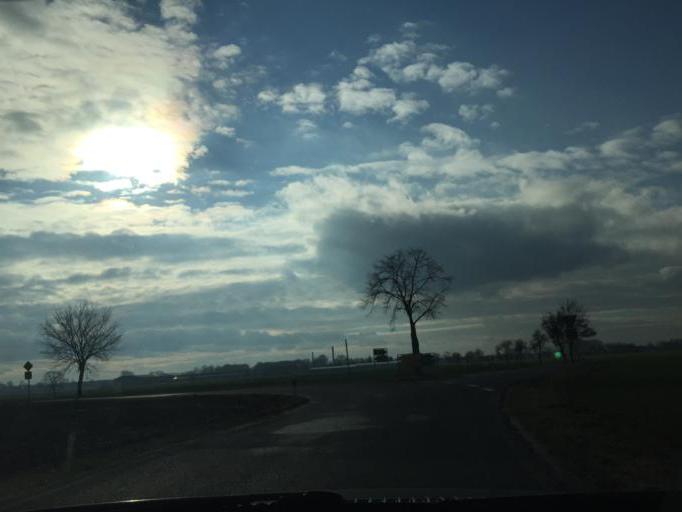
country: DE
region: Saxony
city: Schonfeld
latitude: 51.2783
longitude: 13.6783
